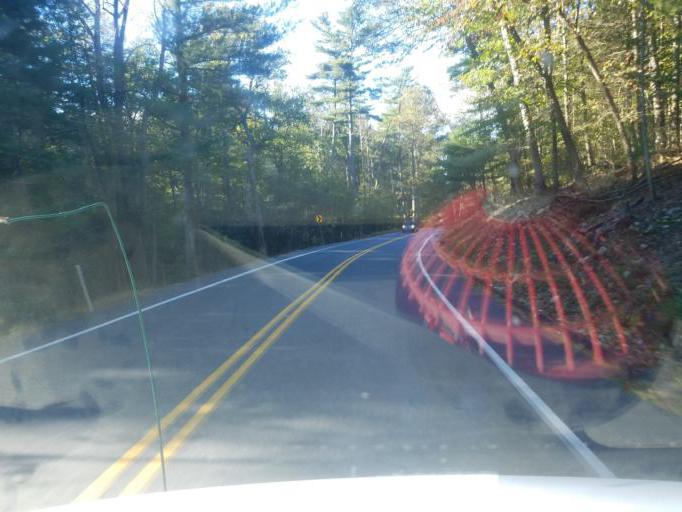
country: US
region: Pennsylvania
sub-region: Franklin County
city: Mont Alto
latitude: 39.8395
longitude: -77.5254
